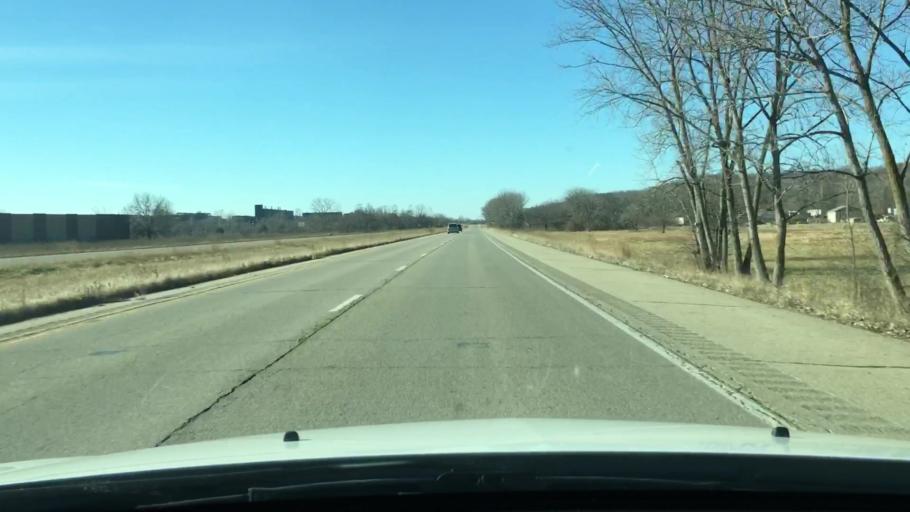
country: US
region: Illinois
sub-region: Peoria County
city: Glasford
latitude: 40.5647
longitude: -89.7352
